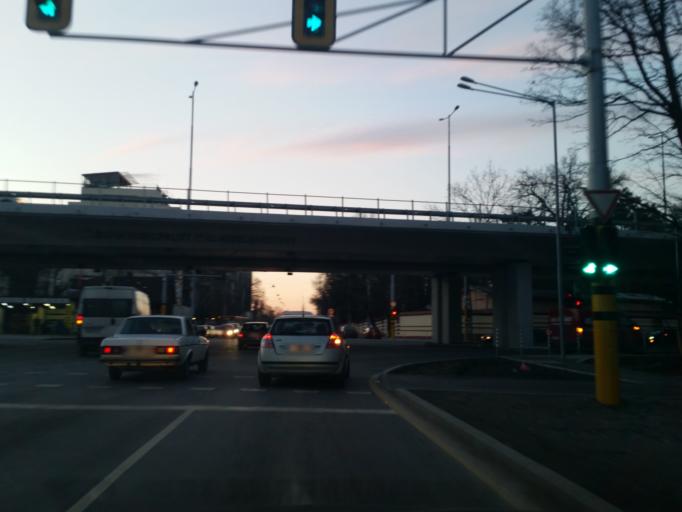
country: BG
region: Sofia-Capital
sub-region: Stolichna Obshtina
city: Sofia
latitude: 42.6723
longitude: 23.3364
